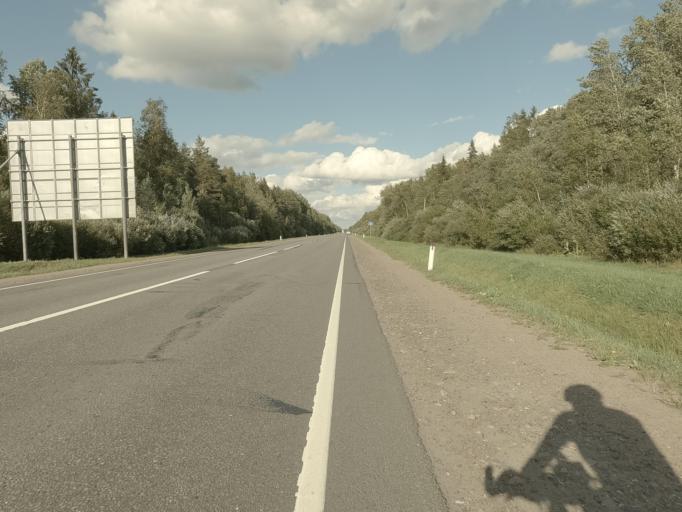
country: RU
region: Leningrad
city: Nikol'skoye
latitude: 59.6478
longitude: 30.8455
